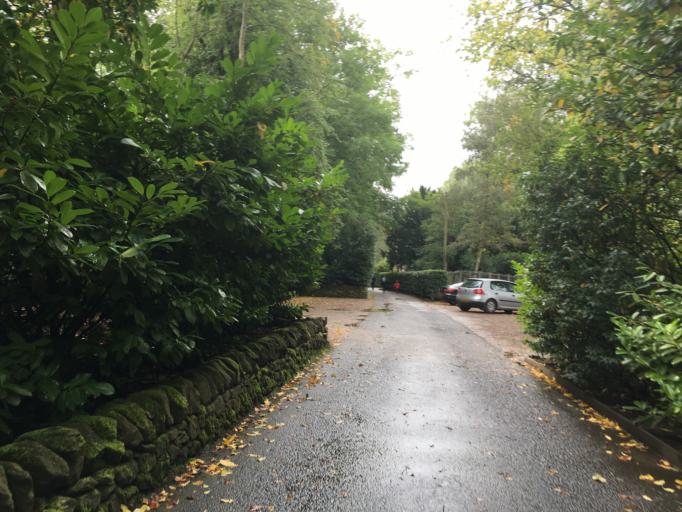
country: GB
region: Scotland
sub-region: West Lothian
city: Kirknewton
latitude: 55.9075
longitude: -3.4228
